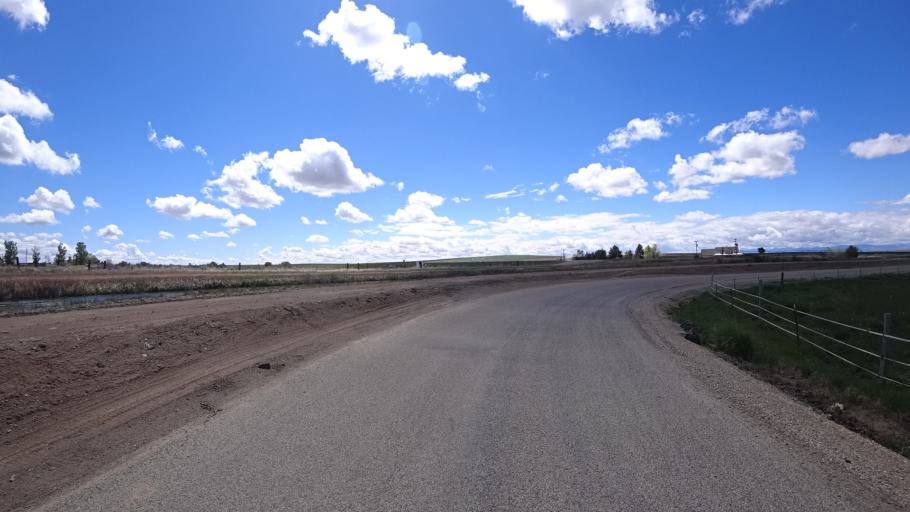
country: US
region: Idaho
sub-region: Ada County
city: Kuna
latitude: 43.4602
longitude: -116.3746
